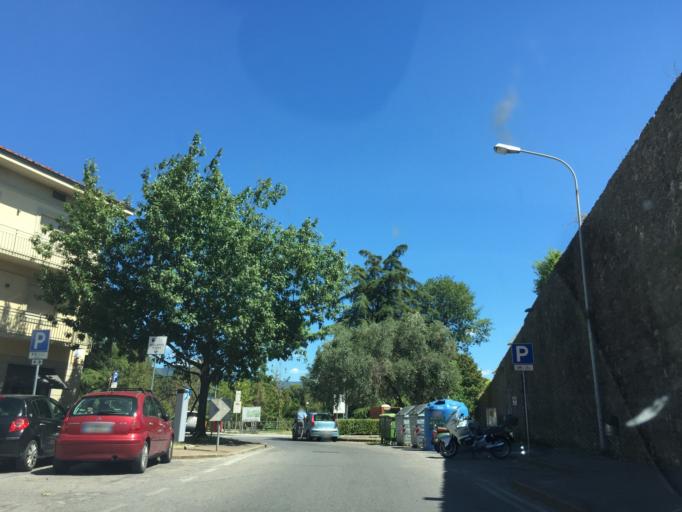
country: IT
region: Tuscany
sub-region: Provincia di Pistoia
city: Pistoia
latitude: 43.9288
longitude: 10.9188
